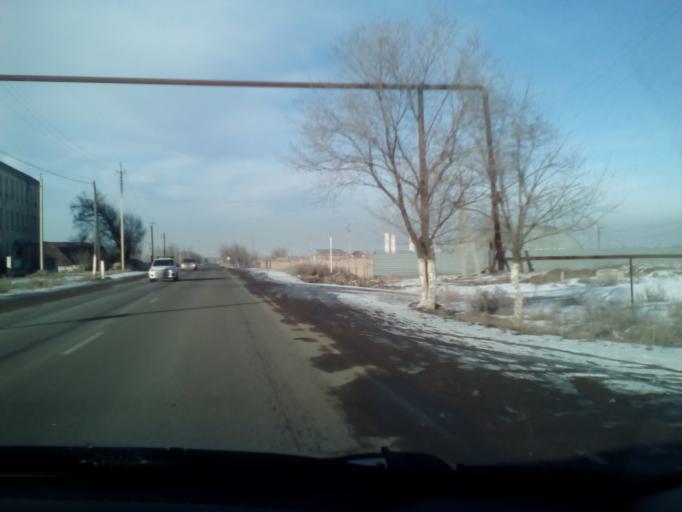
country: KZ
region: Almaty Oblysy
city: Burunday
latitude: 43.1918
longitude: 76.4148
